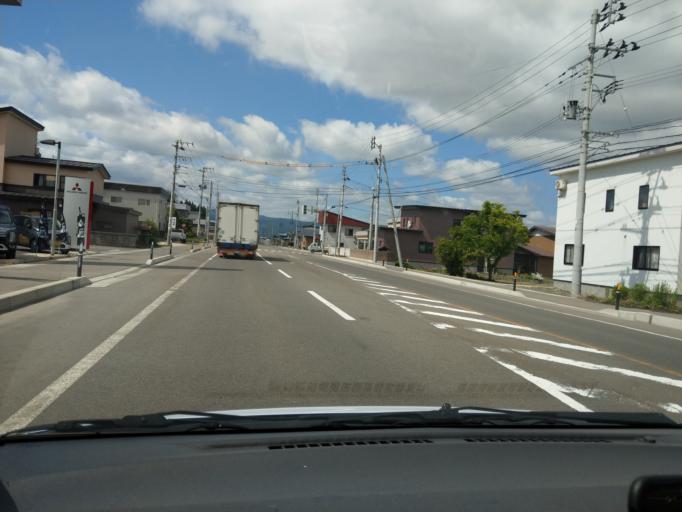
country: JP
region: Akita
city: Yuzawa
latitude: 39.1814
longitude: 140.4961
